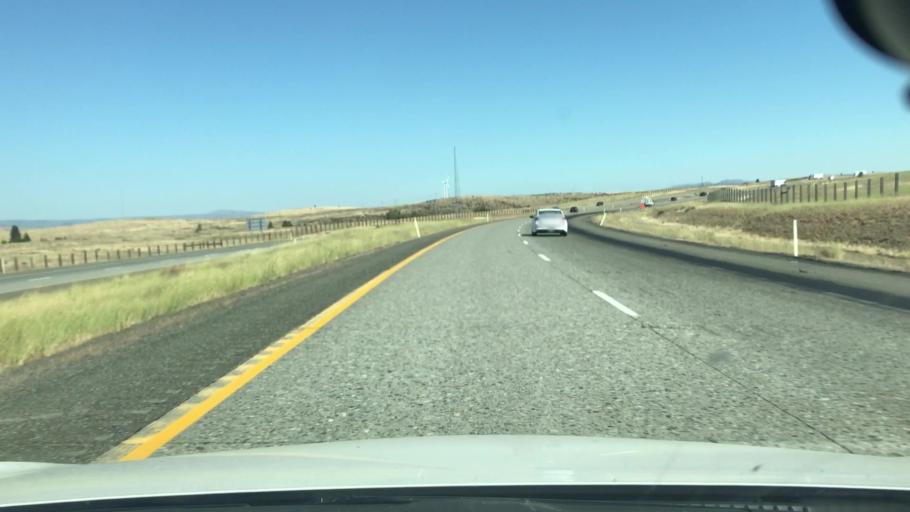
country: US
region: Washington
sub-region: Kittitas County
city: Cle Elum
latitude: 47.1078
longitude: -120.7693
